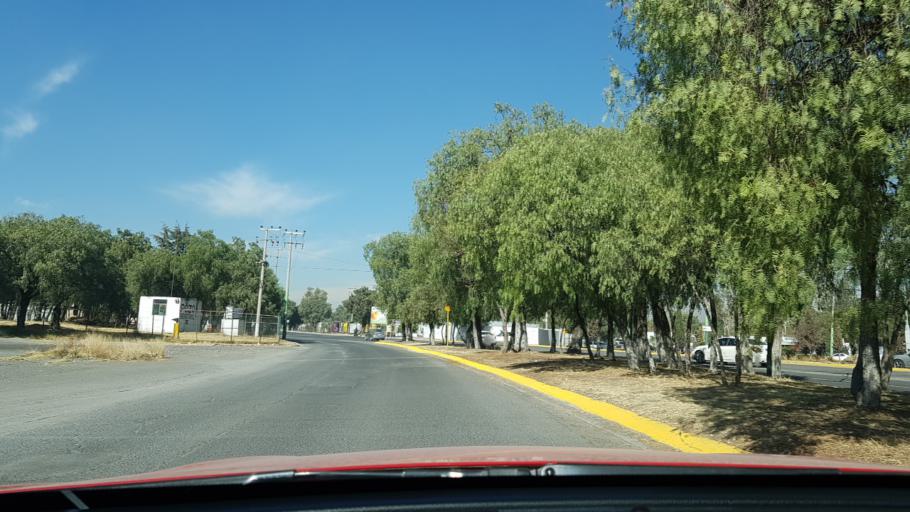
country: MX
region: Mexico
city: Cuautitlan Izcalli
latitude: 19.6577
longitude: -99.2038
